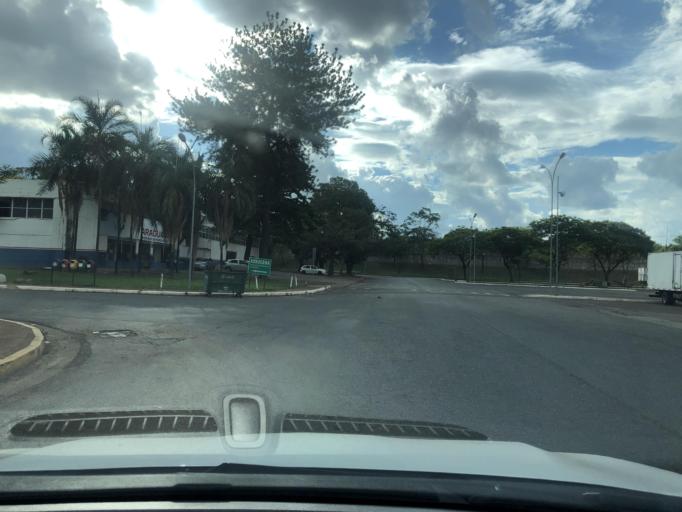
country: BR
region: Federal District
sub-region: Brasilia
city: Brasilia
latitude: -15.7931
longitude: -47.9497
